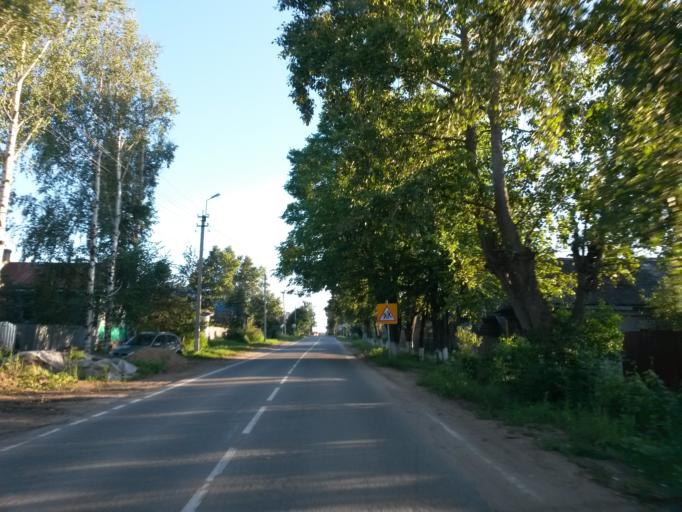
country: RU
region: Jaroslavl
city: Tutayev
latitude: 57.8728
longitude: 39.5244
